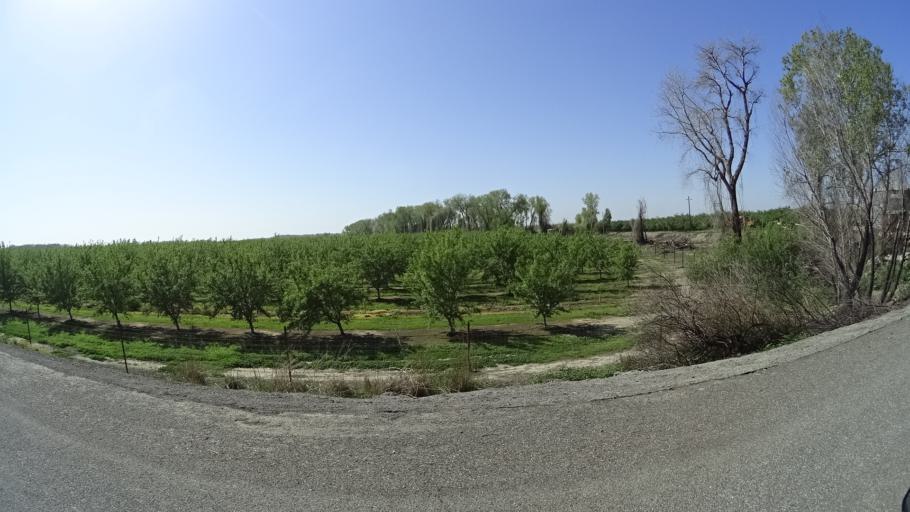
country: US
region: California
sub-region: Glenn County
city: Hamilton City
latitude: 39.6596
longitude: -121.9988
